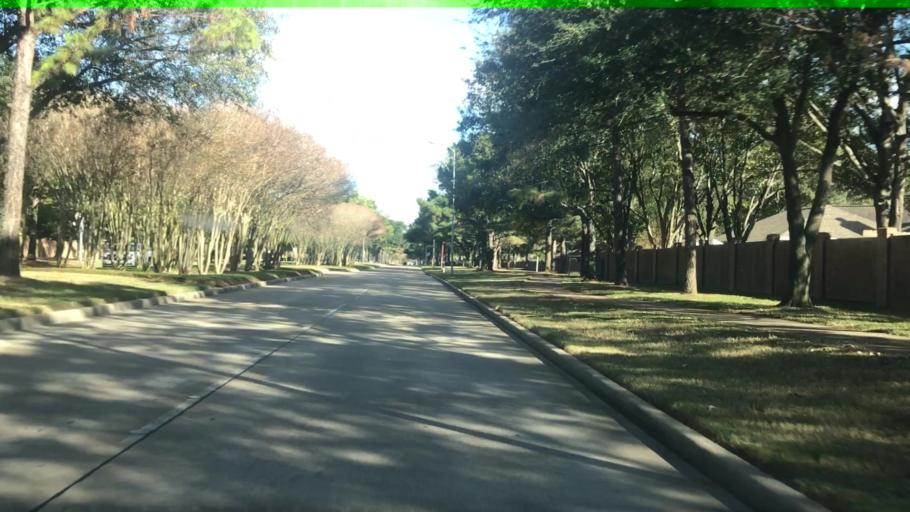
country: US
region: Texas
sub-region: Fort Bend County
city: Cinco Ranch
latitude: 29.7572
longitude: -95.7718
